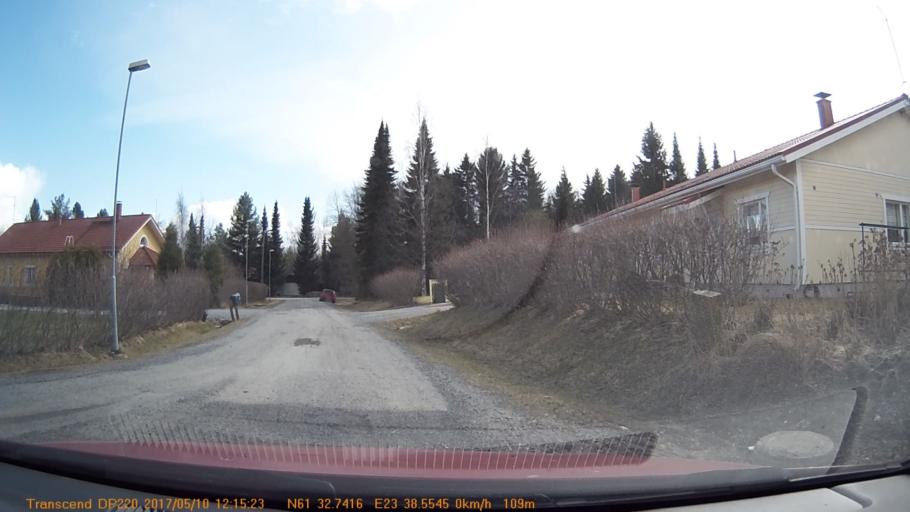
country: FI
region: Pirkanmaa
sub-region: Tampere
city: Yloejaervi
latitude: 61.5457
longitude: 23.6426
